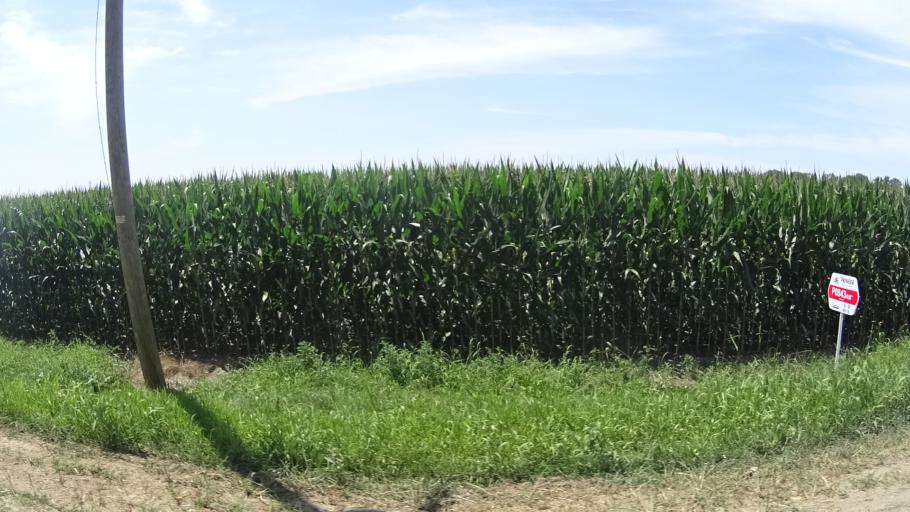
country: US
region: Ohio
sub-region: Erie County
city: Sandusky
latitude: 41.4210
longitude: -82.7720
